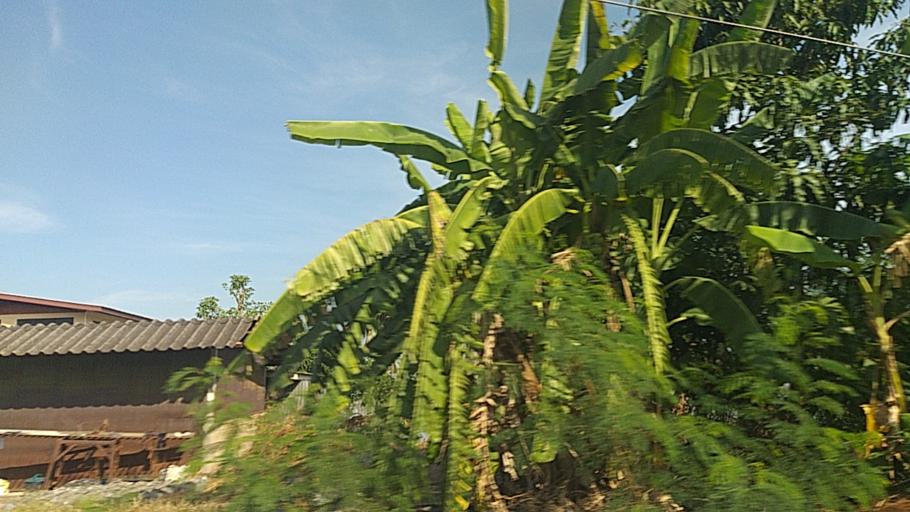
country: TH
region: Pathum Thani
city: Thanyaburi
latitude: 13.9997
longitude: 100.7307
